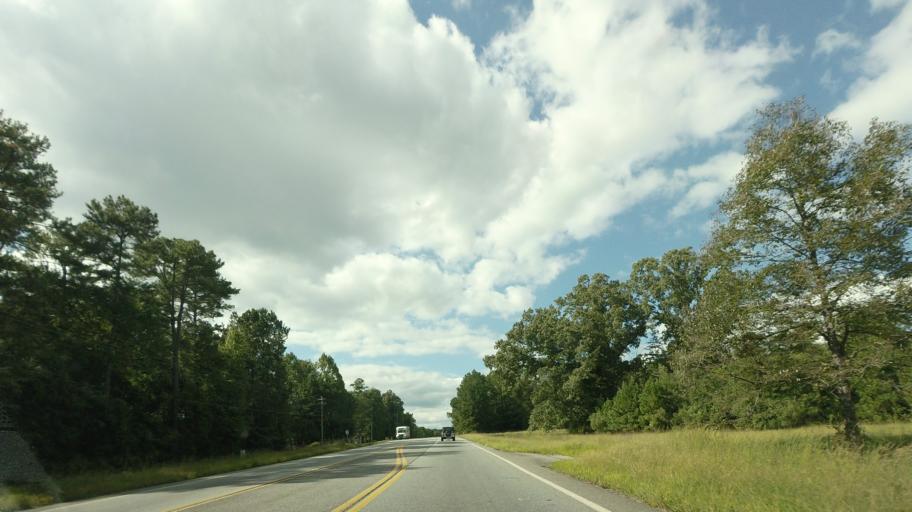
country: US
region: Georgia
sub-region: Bibb County
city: Macon
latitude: 32.9415
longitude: -83.7207
